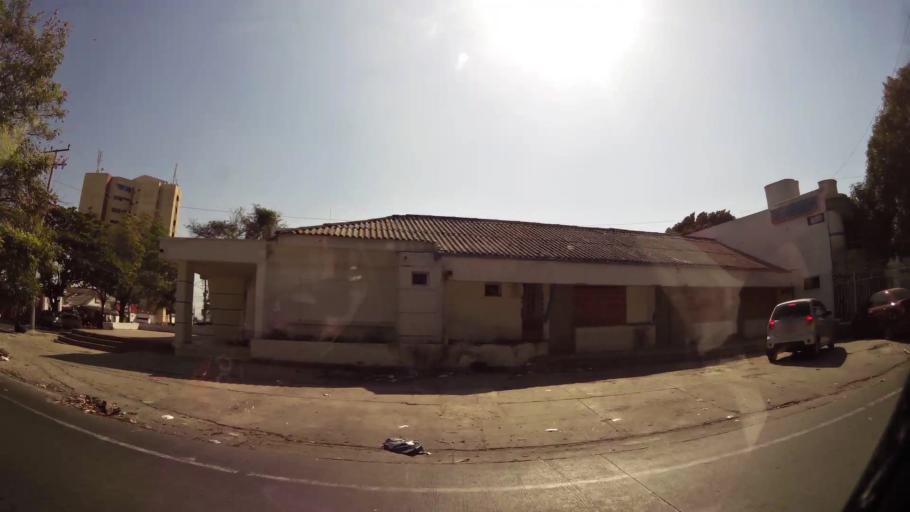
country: CO
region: Atlantico
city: Barranquilla
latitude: 10.9915
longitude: -74.7904
